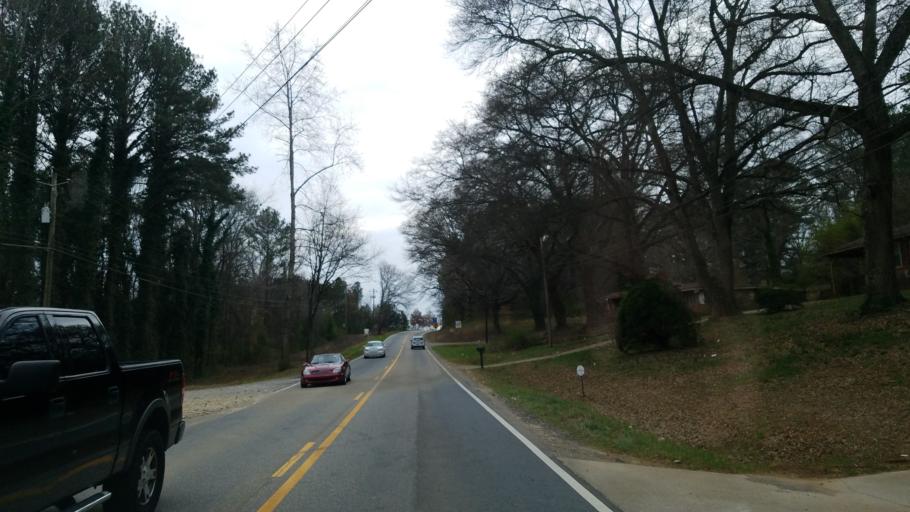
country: US
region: Georgia
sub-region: Cherokee County
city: Canton
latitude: 34.2624
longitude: -84.4619
